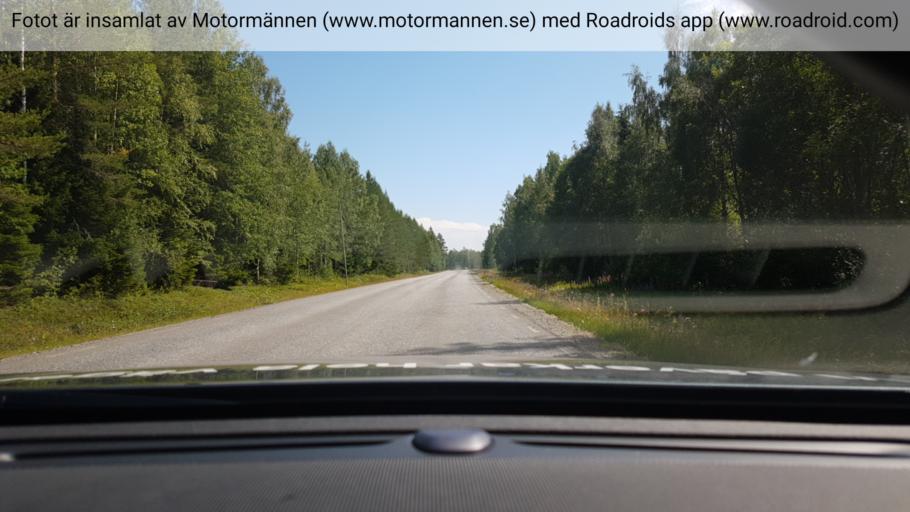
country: SE
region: Vaesterbotten
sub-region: Robertsfors Kommun
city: Robertsfors
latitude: 64.2010
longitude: 20.8298
